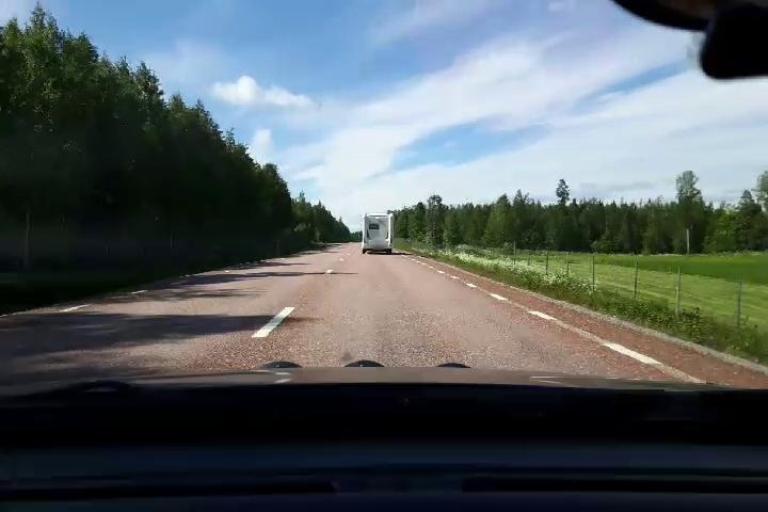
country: SE
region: Gaevleborg
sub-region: Bollnas Kommun
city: Kilafors
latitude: 61.2089
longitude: 16.7427
